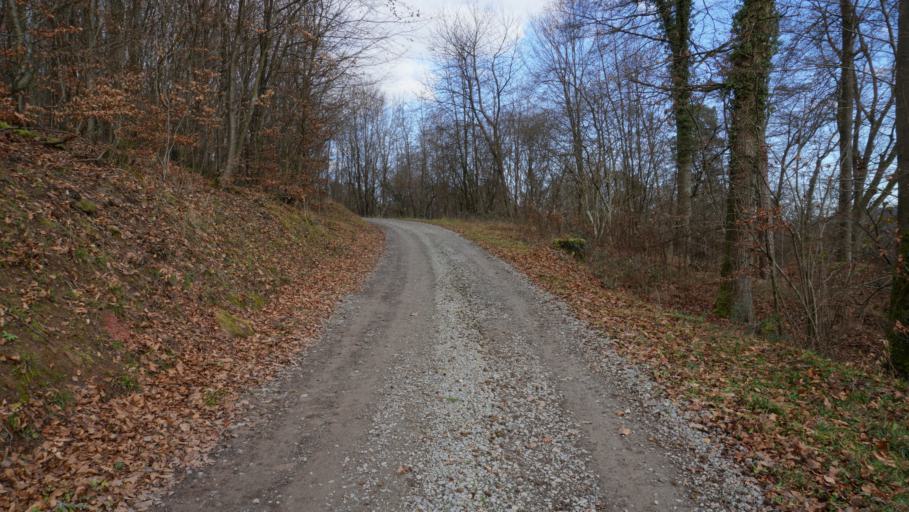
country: DE
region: Baden-Wuerttemberg
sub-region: Karlsruhe Region
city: Neckargerach
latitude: 49.4044
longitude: 9.0734
